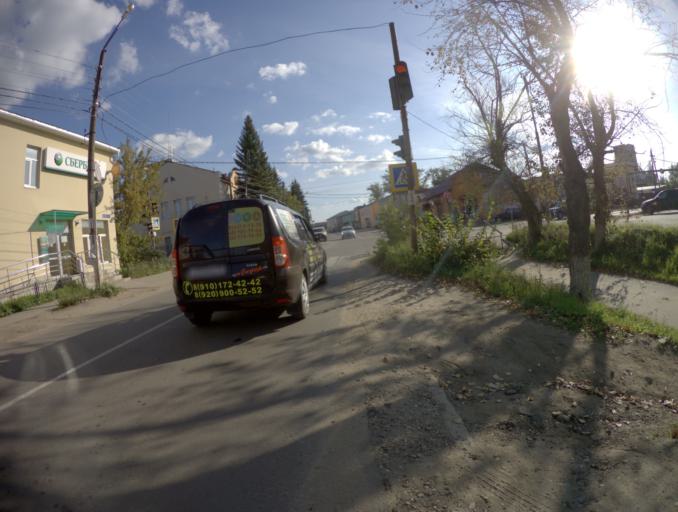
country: RU
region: Vladimir
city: Petushki
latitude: 55.9274
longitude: 39.4647
